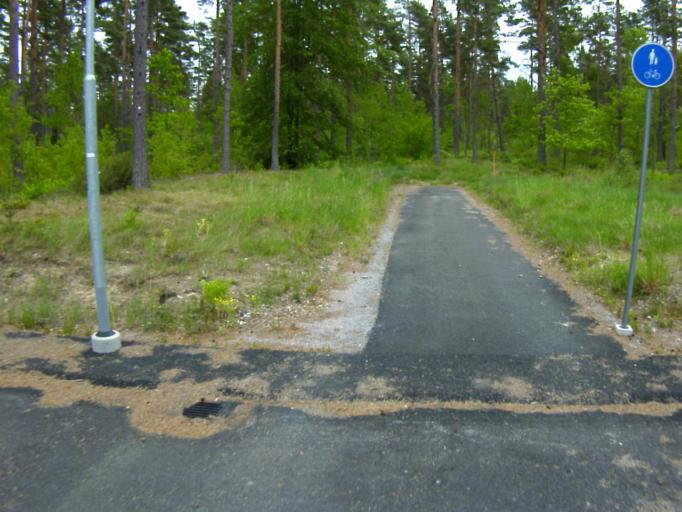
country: SE
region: Skane
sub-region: Kristianstads Kommun
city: Ahus
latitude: 55.9482
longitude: 14.2905
